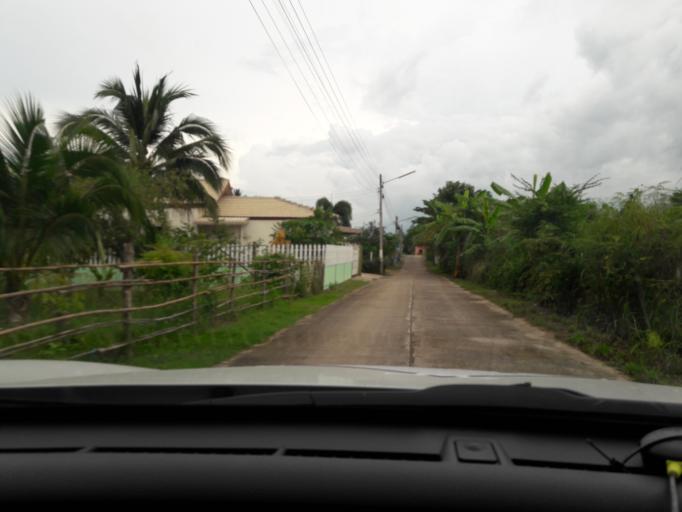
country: TH
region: Nakhon Sawan
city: Tak Fa
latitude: 15.3530
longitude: 100.4985
